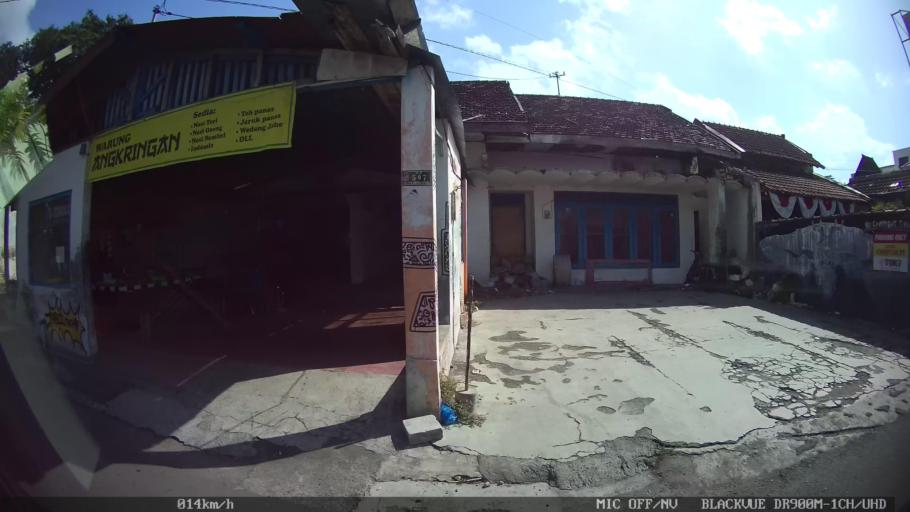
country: ID
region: Daerah Istimewa Yogyakarta
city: Yogyakarta
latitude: -7.8199
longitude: 110.3697
